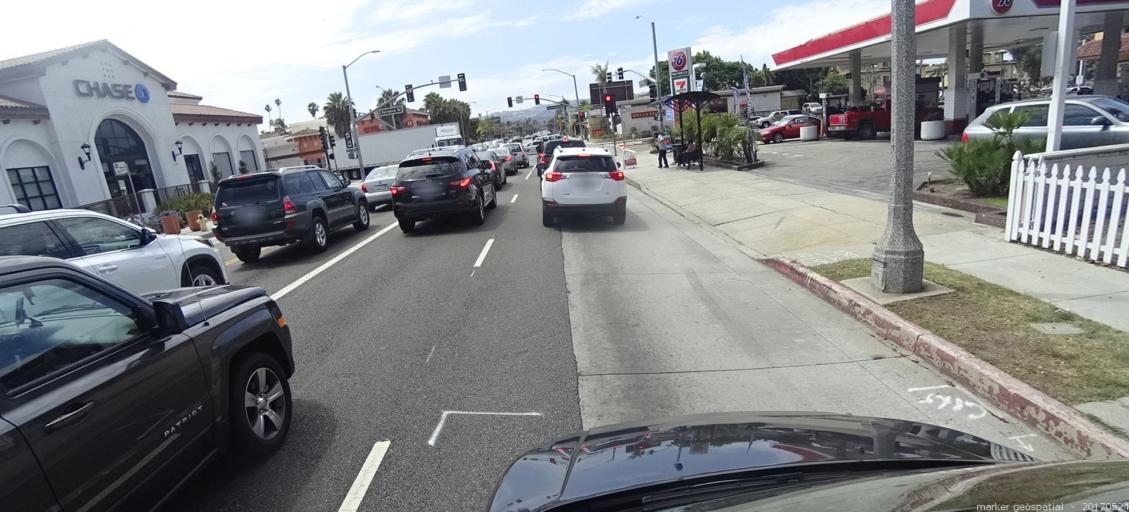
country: US
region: California
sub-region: Los Angeles County
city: Redondo Beach
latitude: 33.8388
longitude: -118.3856
